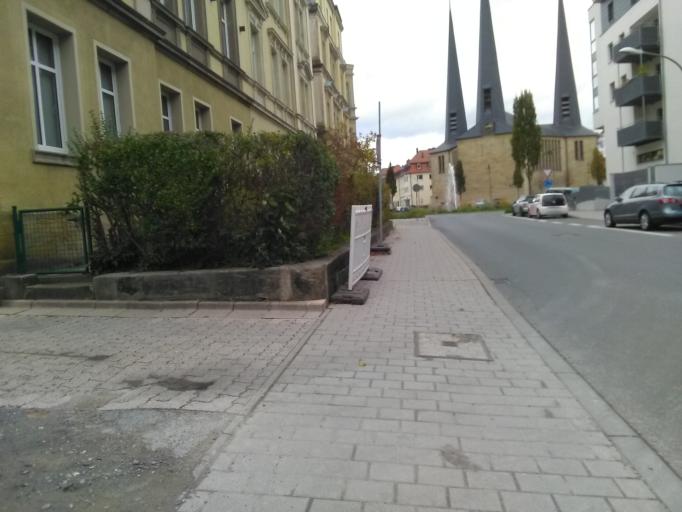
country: DE
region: Bavaria
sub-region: Upper Franconia
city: Bayreuth
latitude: 49.9502
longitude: 11.5764
